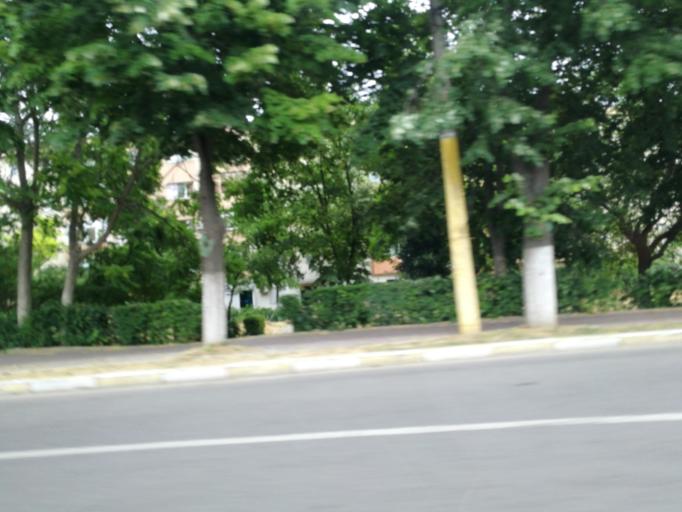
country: RO
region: Constanta
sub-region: Municipiul Constanta
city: Constanta
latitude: 44.1975
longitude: 28.6317
